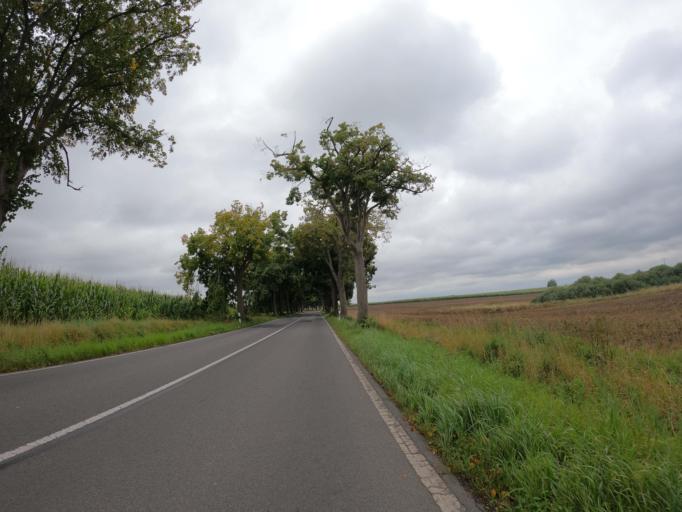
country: DE
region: Mecklenburg-Vorpommern
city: Garz
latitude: 54.3160
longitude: 13.3366
